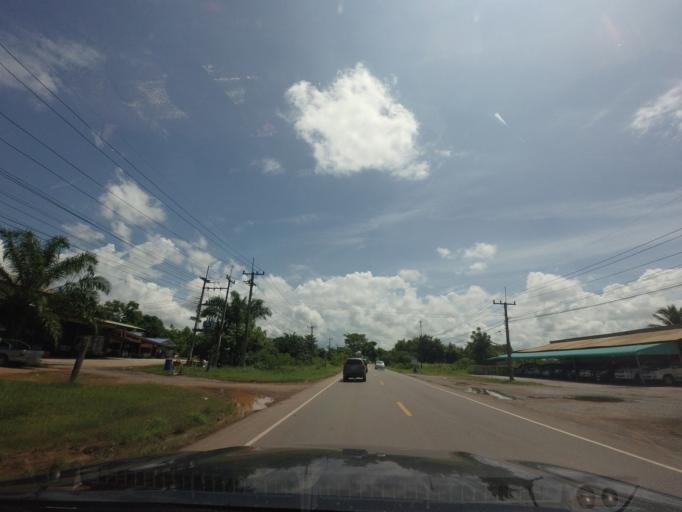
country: TH
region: Changwat Udon Thani
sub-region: Amphoe Ban Phue
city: Ban Phue
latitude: 17.6972
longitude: 102.4516
